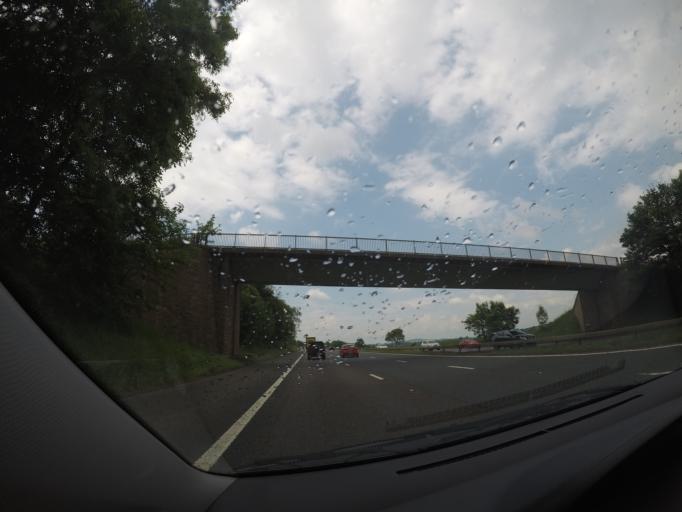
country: GB
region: England
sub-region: Cumbria
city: Penrith
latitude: 54.7493
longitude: -2.8154
